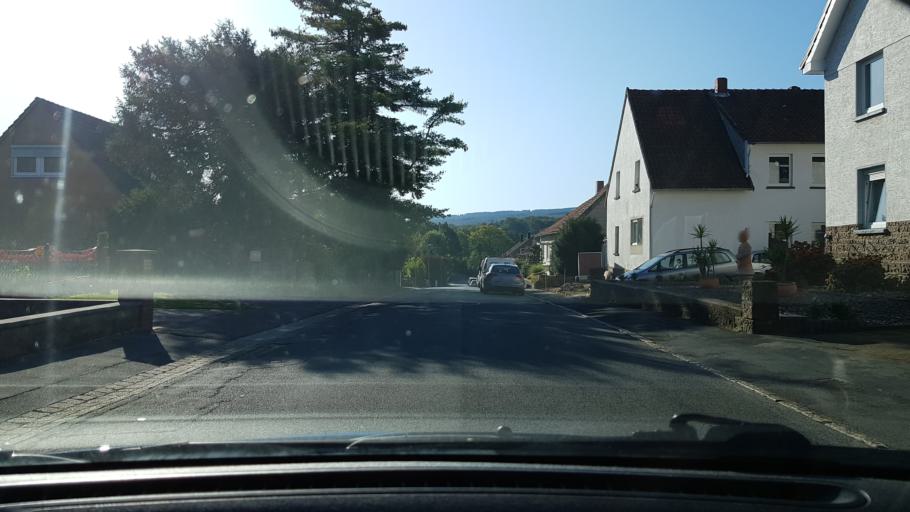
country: DE
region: Lower Saxony
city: Egestorf
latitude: 52.2870
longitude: 9.5025
